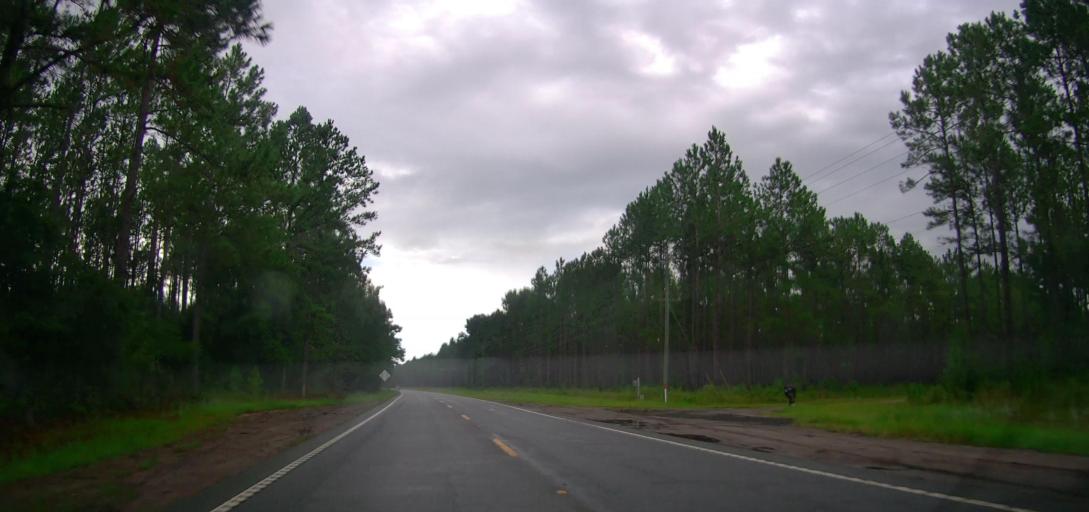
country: US
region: Georgia
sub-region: Ware County
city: Deenwood
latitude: 31.2661
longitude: -82.5202
